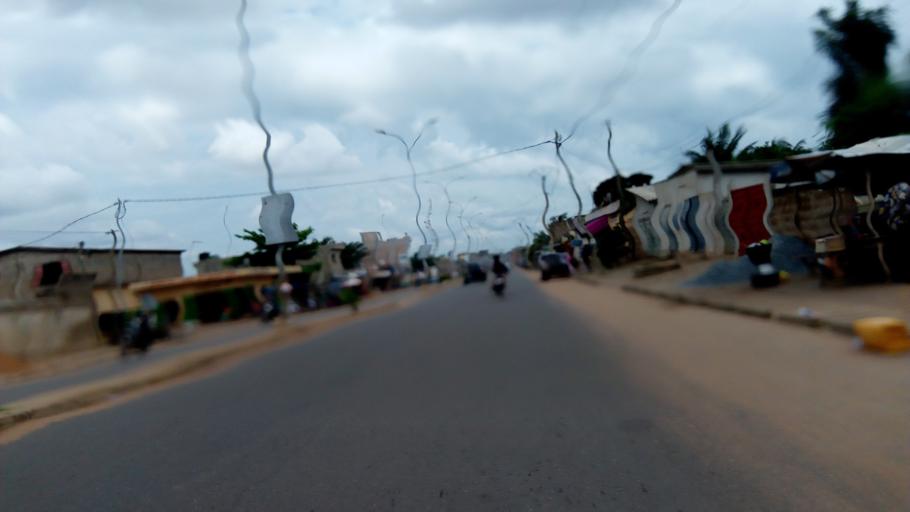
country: TG
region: Maritime
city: Lome
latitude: 6.2087
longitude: 1.1805
